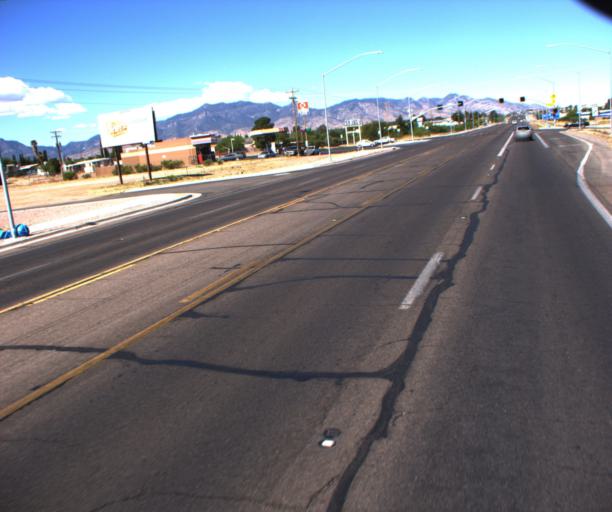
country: US
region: Arizona
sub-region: Cochise County
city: Sierra Vista
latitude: 31.5547
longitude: -110.2428
